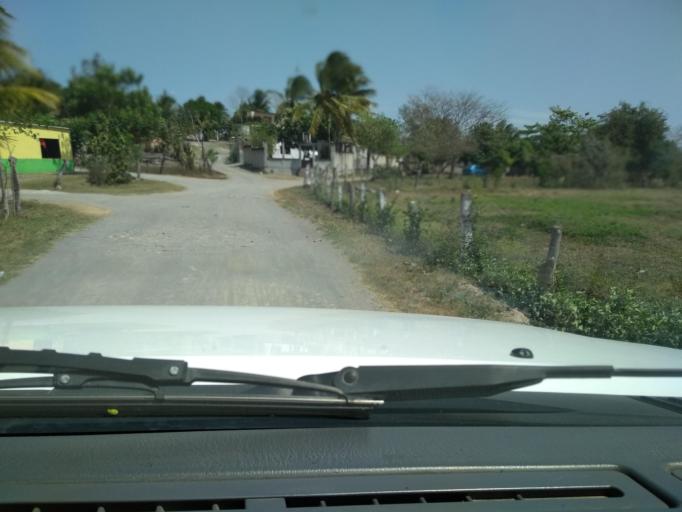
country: MX
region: Veracruz
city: Manlio Fabio Altamirano
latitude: 19.1550
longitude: -96.3295
